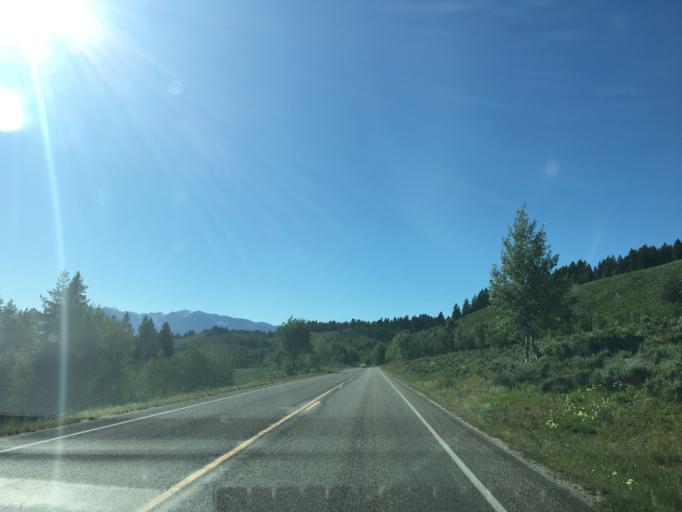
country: US
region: Wyoming
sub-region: Teton County
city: Jackson
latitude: 43.8629
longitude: -110.5358
